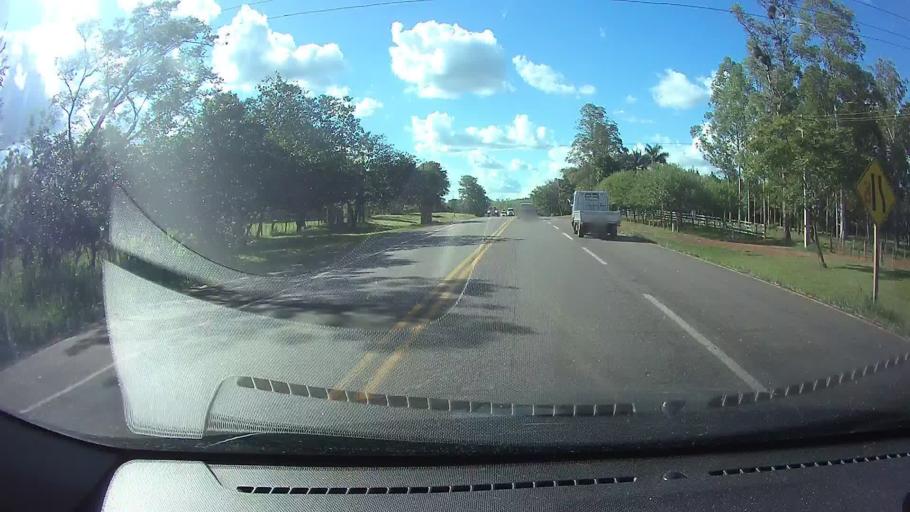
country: PY
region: Cordillera
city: Itacurubi de la Cordillera
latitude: -25.4416
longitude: -56.9058
